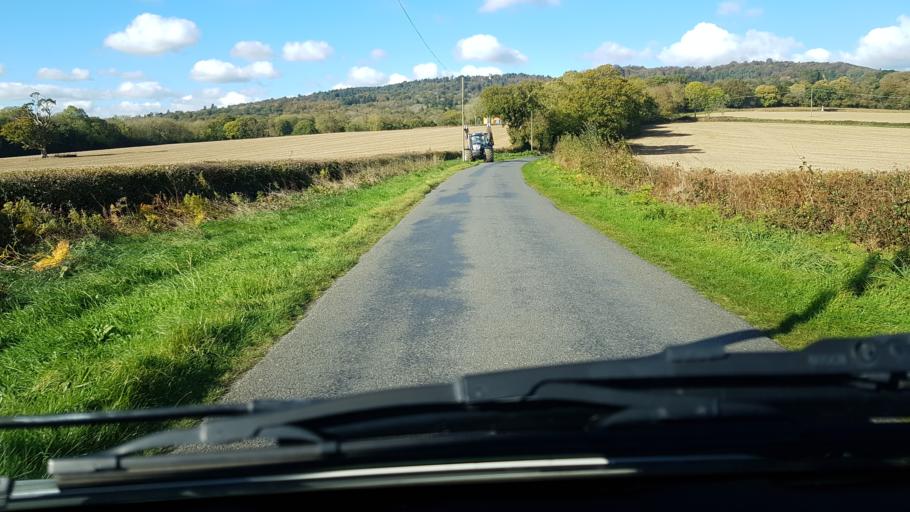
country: GB
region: England
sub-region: Surrey
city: Ockley
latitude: 51.1627
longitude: -0.3549
